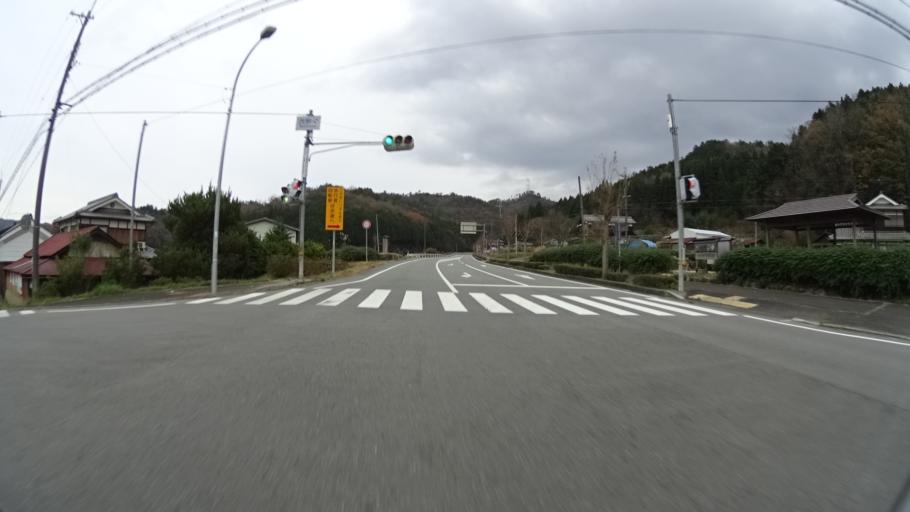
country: JP
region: Hyogo
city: Sasayama
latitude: 35.0748
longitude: 135.3749
